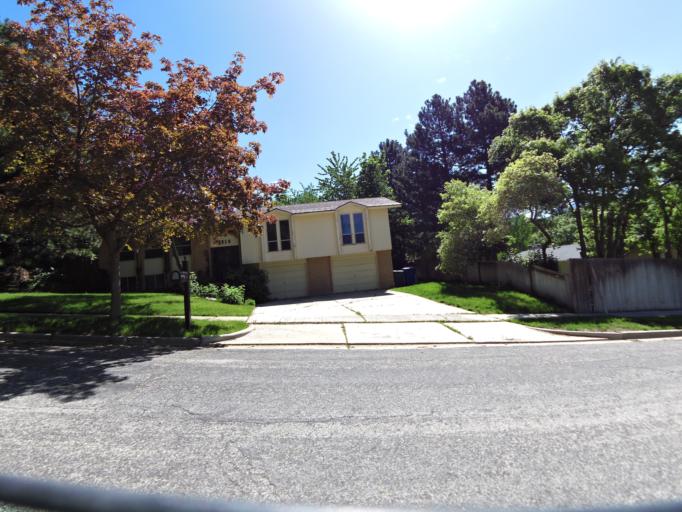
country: US
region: Utah
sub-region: Weber County
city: Uintah
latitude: 41.1688
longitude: -111.9369
